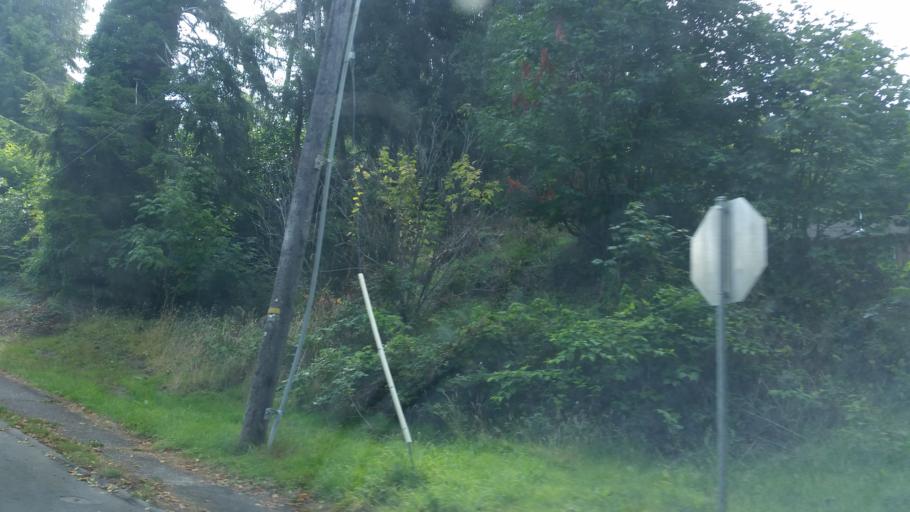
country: US
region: Oregon
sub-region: Clatsop County
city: Astoria
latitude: 46.1856
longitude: -123.8170
